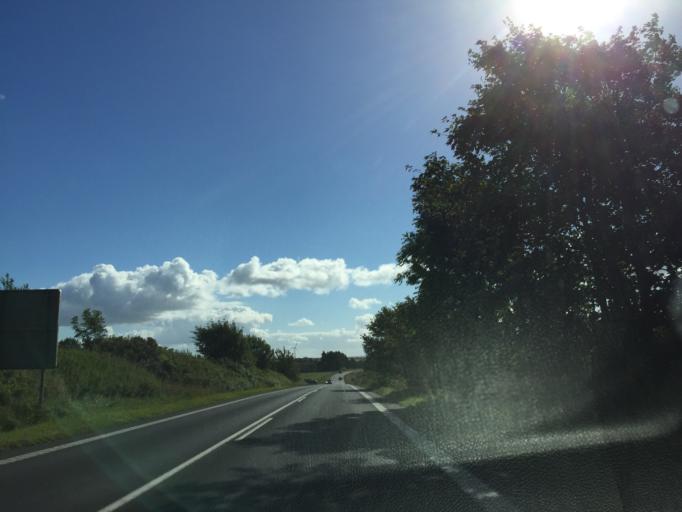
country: DK
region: Central Jutland
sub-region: Viborg Kommune
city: Bjerringbro
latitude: 56.3523
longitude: 9.6777
